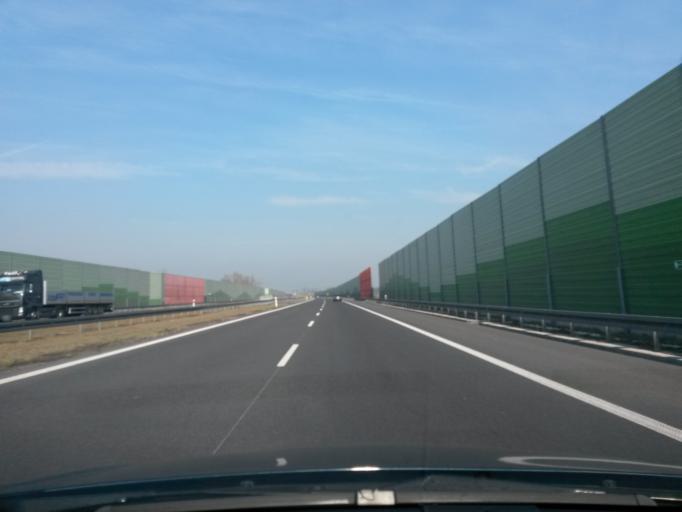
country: PL
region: Lodz Voivodeship
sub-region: Powiat leczycki
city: Piatek
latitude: 52.1151
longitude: 19.5050
